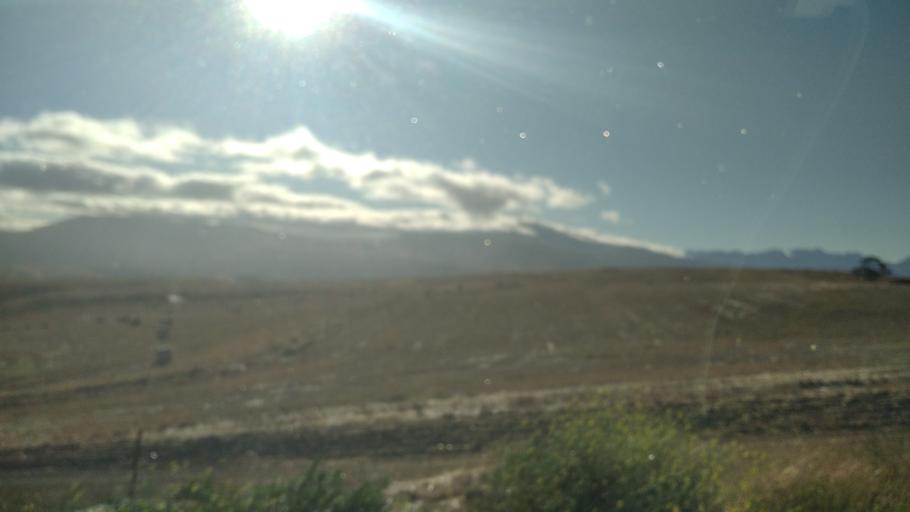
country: ZA
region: Western Cape
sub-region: Overberg District Municipality
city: Caledon
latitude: -34.1468
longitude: 19.2992
